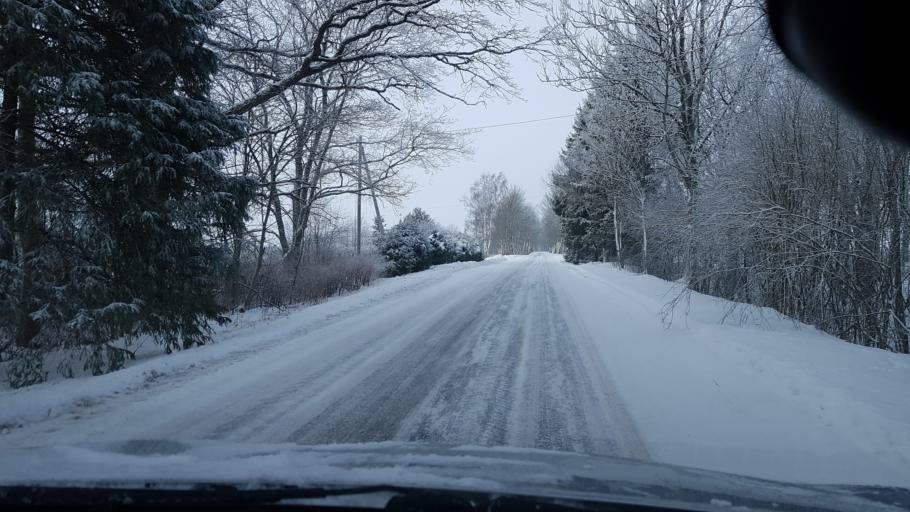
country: EE
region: Harju
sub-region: Keila linn
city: Keila
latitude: 59.3276
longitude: 24.4481
